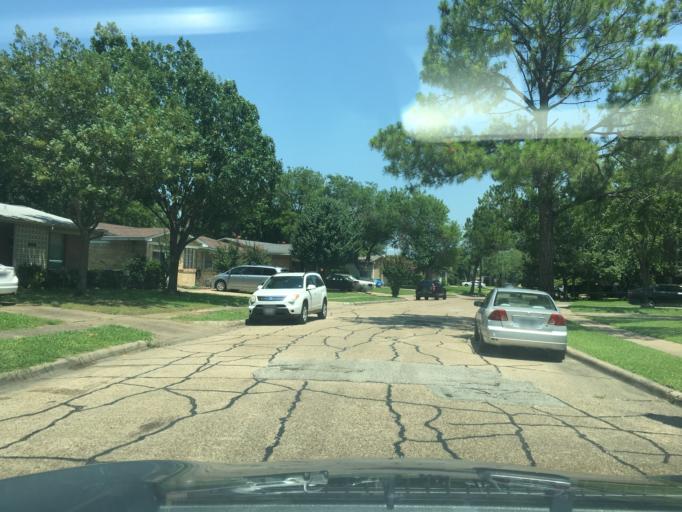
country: US
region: Texas
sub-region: Dallas County
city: Richardson
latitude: 32.9216
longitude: -96.7024
